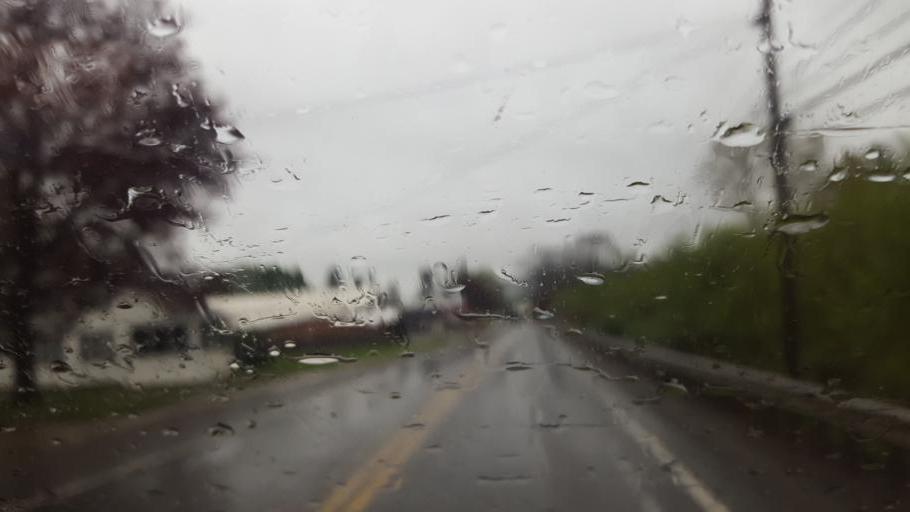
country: US
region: Pennsylvania
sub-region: Tioga County
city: Westfield
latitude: 41.9180
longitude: -77.5485
